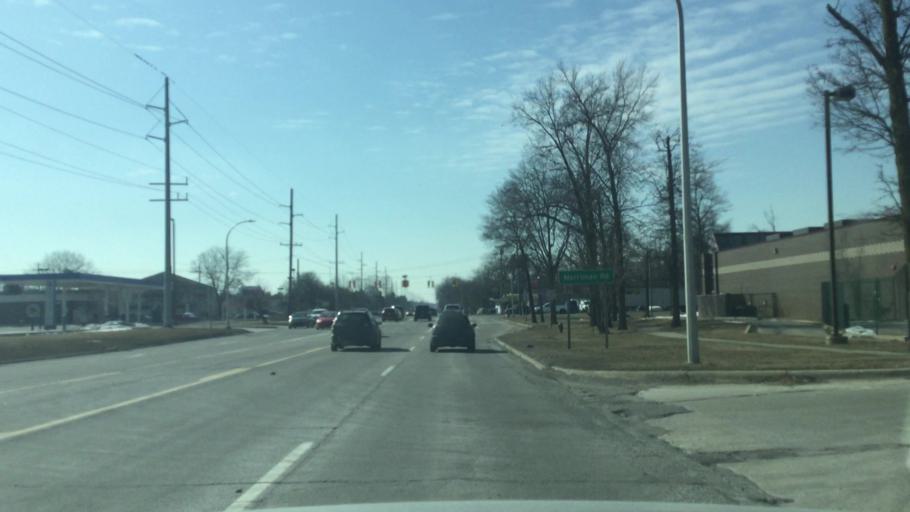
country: US
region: Michigan
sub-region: Wayne County
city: Garden City
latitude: 42.3103
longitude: -83.3475
